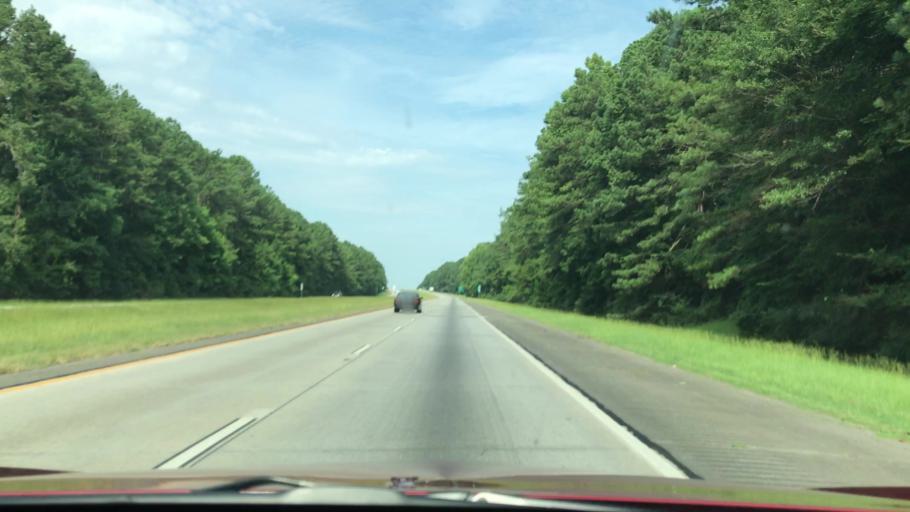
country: US
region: Georgia
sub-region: Warren County
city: Firing Range
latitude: 33.5005
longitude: -82.7901
